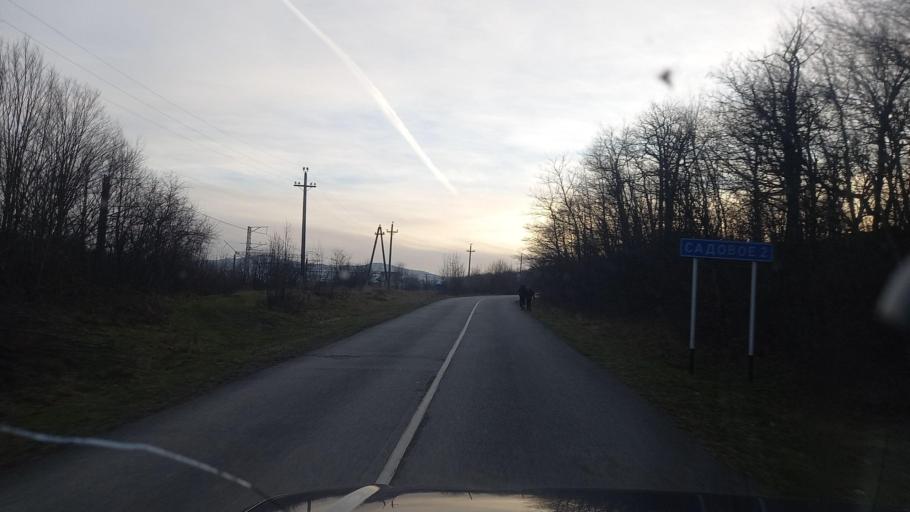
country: RU
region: Krasnodarskiy
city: Goryachiy Klyuch
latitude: 44.3899
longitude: 39.1920
